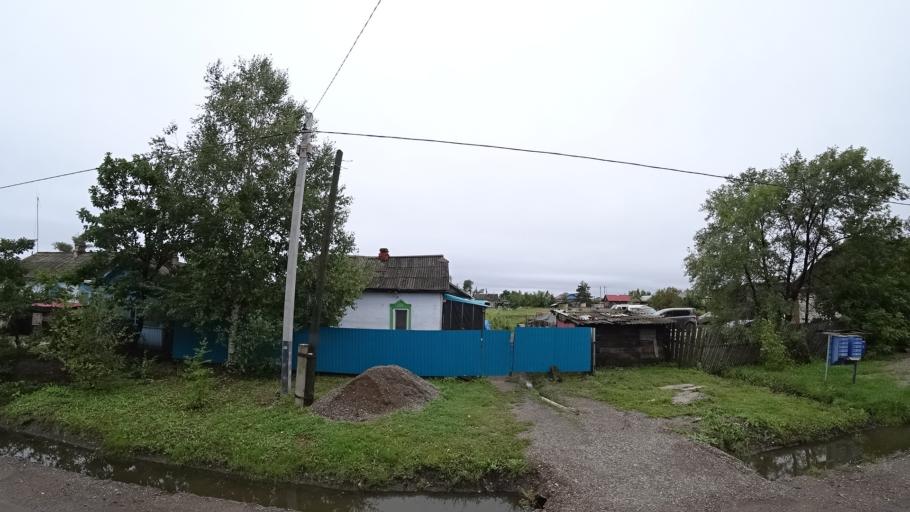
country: RU
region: Primorskiy
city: Monastyrishche
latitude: 44.2090
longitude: 132.4354
